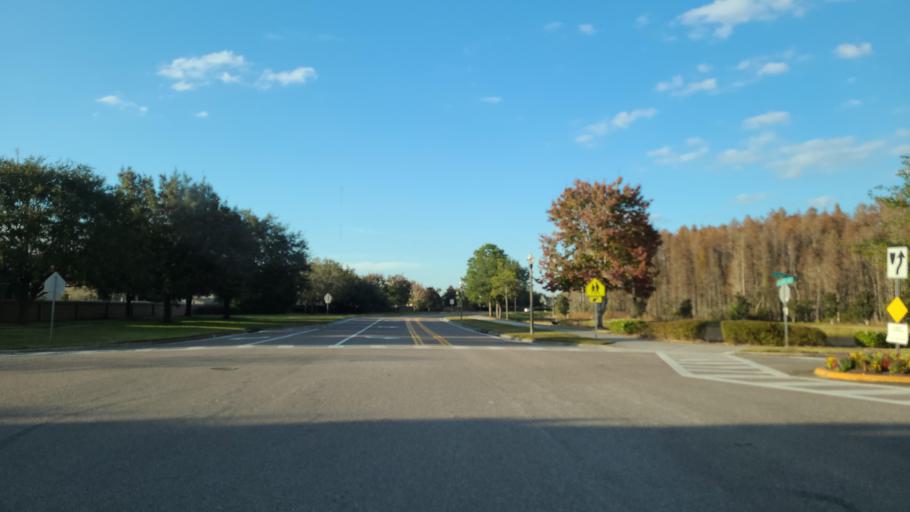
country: US
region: Florida
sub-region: Hillsborough County
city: Cheval
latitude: 28.2069
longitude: -82.5237
